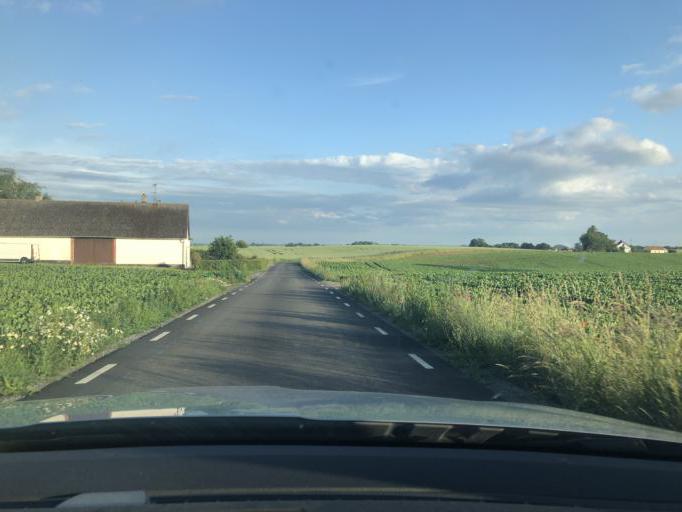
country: SE
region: Skane
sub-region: Simrishamns Kommun
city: Simrishamn
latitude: 55.4684
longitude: 14.1913
